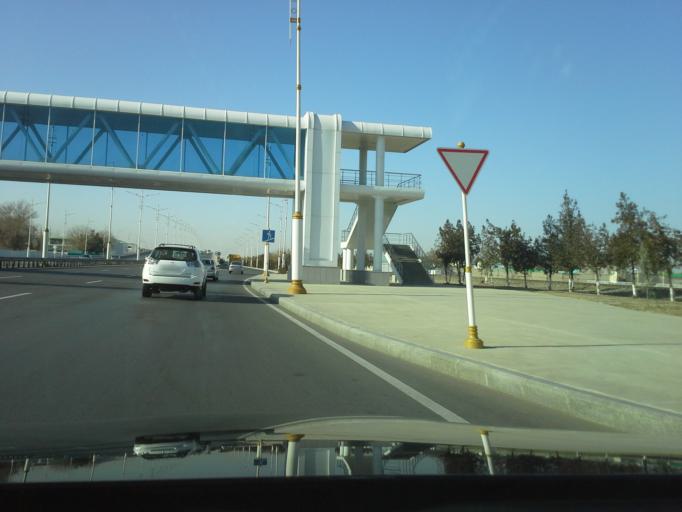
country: TM
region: Ahal
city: Ashgabat
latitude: 37.9594
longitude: 58.3666
